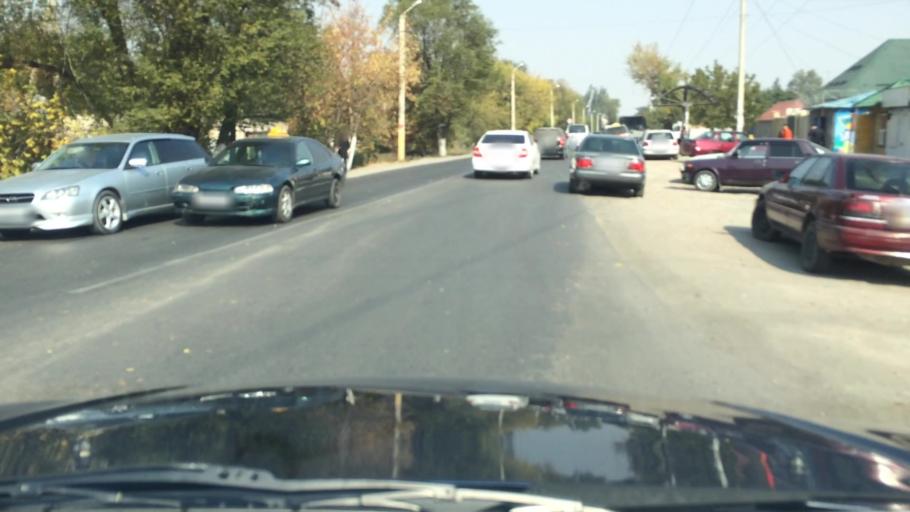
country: KG
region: Chuy
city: Lebedinovka
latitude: 42.8860
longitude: 74.6787
